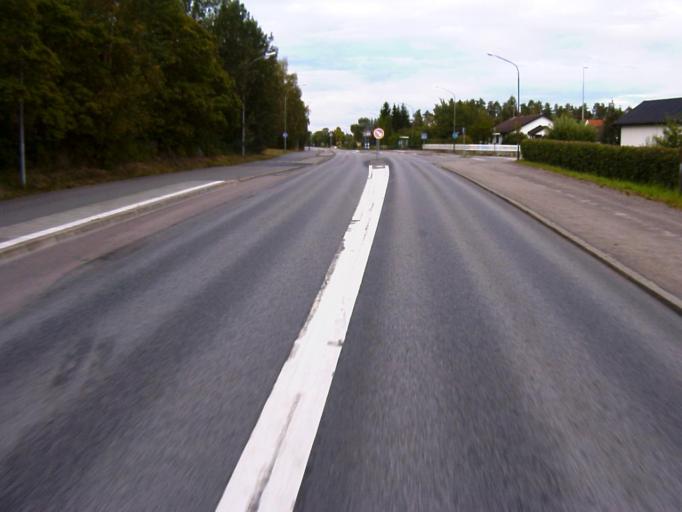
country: SE
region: Soedermanland
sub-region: Eskilstuna Kommun
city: Torshalla
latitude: 59.3997
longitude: 16.4866
